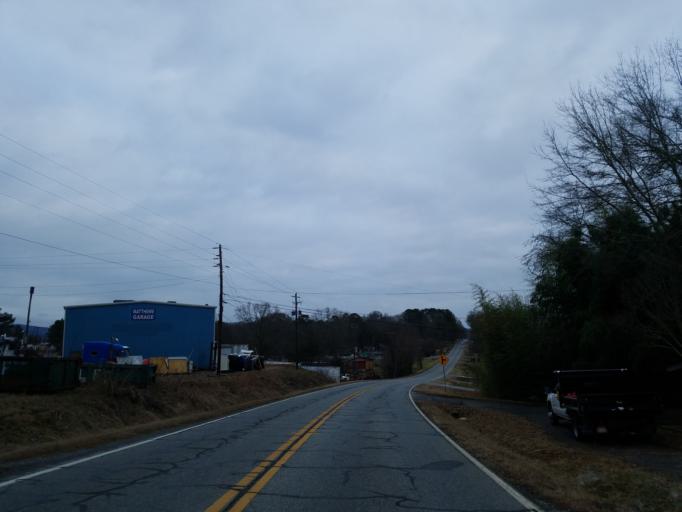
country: US
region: Georgia
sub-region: Bartow County
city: Cartersville
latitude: 34.2116
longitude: -84.8350
